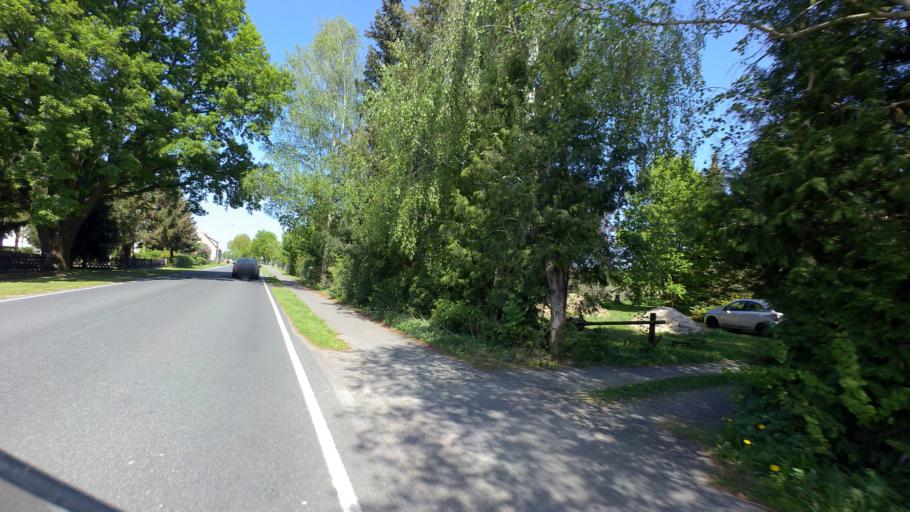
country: DE
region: Brandenburg
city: Schlepzig
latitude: 52.0837
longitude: 13.8936
